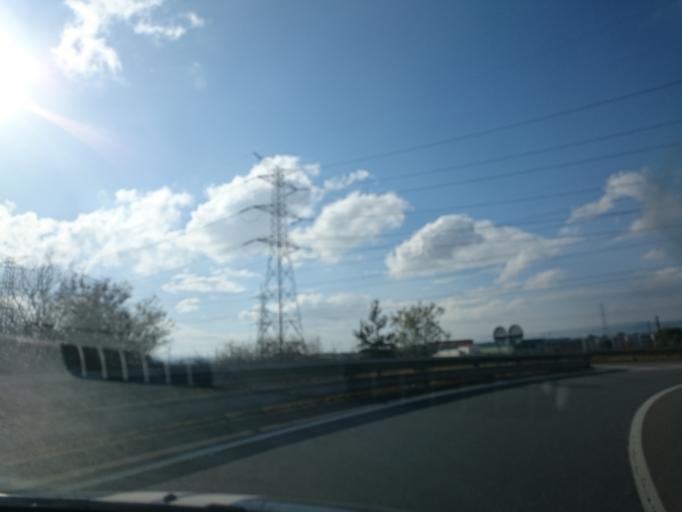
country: ES
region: Catalonia
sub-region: Provincia de Barcelona
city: Vic
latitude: 41.9562
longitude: 2.2860
